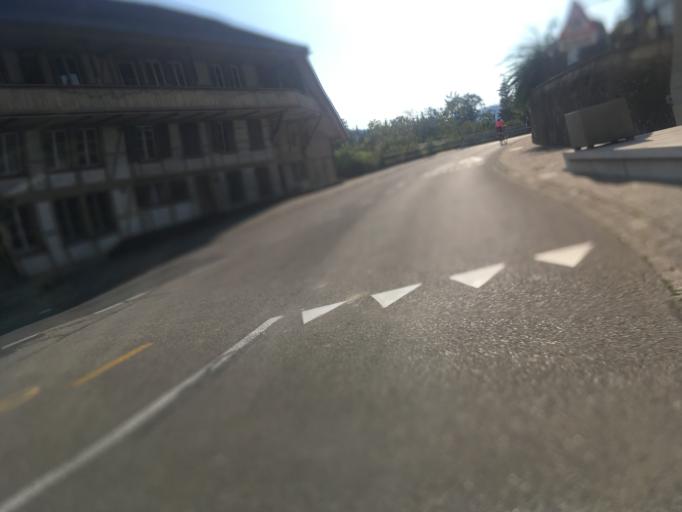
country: CH
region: Bern
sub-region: Emmental District
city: Lutzelfluh
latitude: 47.0082
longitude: 7.6865
